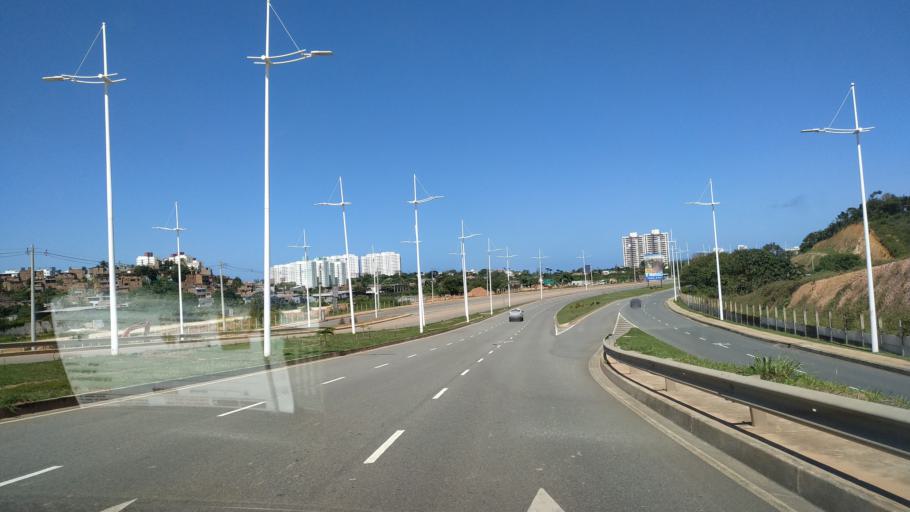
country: BR
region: Bahia
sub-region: Lauro De Freitas
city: Lauro de Freitas
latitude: -12.9290
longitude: -38.3816
